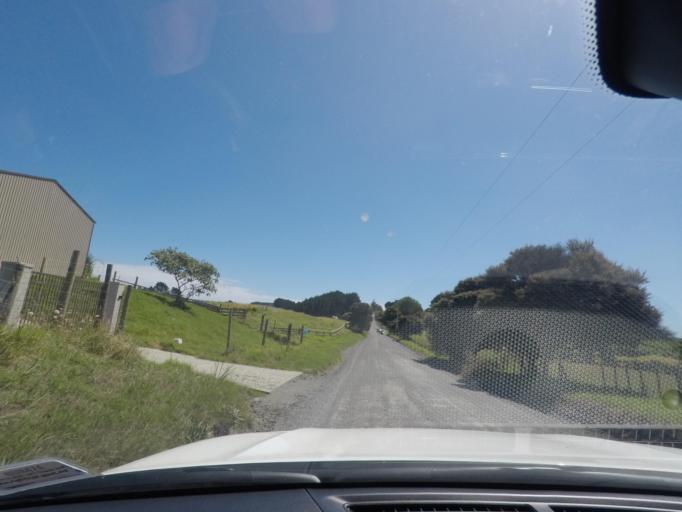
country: NZ
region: Auckland
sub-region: Auckland
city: Parakai
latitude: -36.5793
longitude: 174.3230
